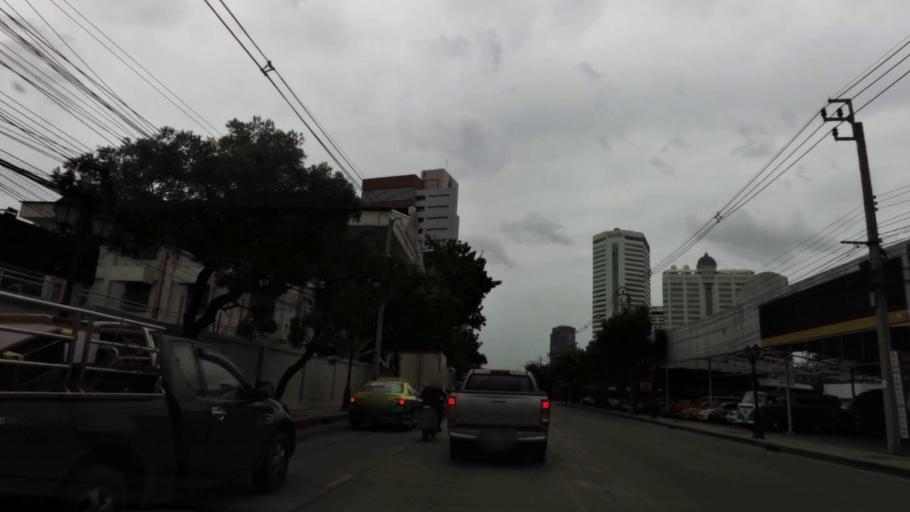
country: TH
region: Bangkok
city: Huai Khwang
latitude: 13.7581
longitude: 100.5728
